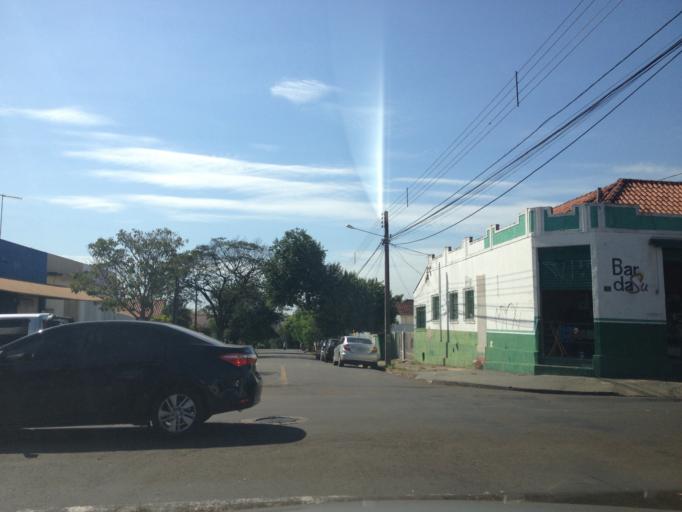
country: BR
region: Parana
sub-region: Londrina
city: Londrina
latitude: -23.3000
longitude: -51.1616
